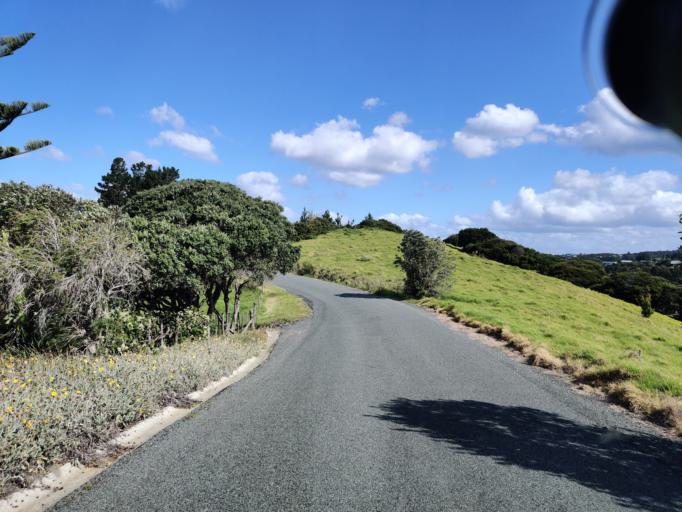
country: NZ
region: Northland
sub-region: Whangarei
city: Ngunguru
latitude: -35.6071
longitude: 174.5268
